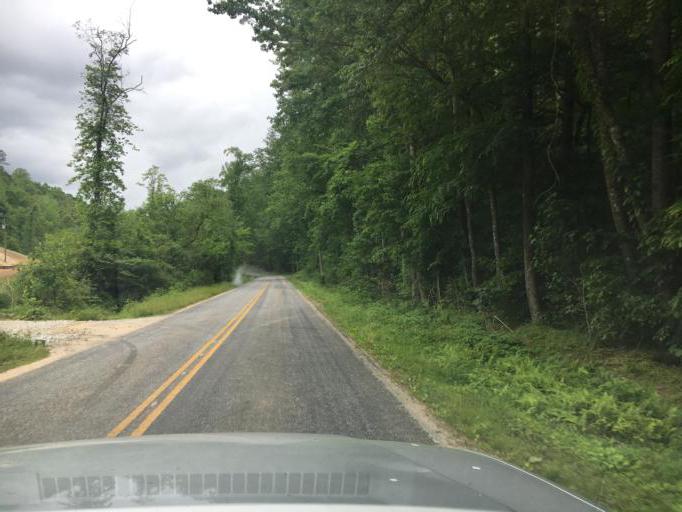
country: US
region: South Carolina
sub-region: Greenville County
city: Tigerville
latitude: 35.1319
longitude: -82.3970
